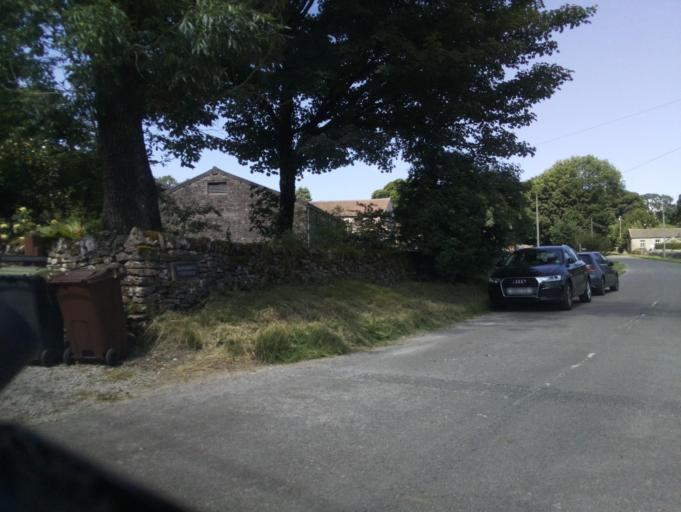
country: GB
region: England
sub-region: Derbyshire
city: Tideswell
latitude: 53.2657
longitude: -1.8175
